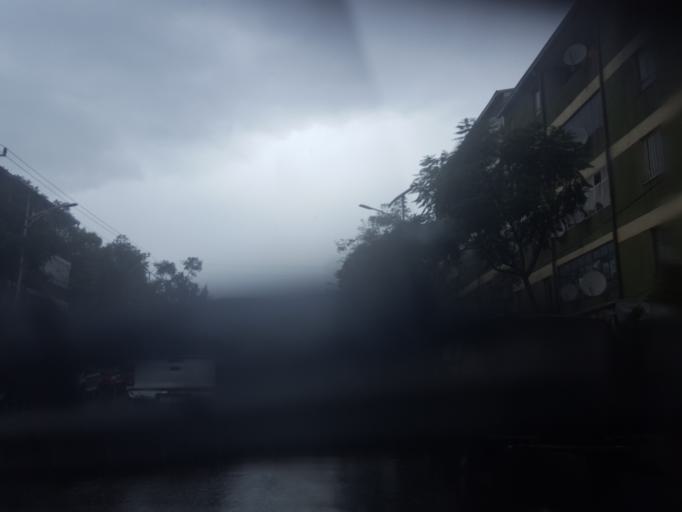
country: ET
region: Adis Abeba
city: Addis Ababa
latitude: 9.0260
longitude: 38.7820
